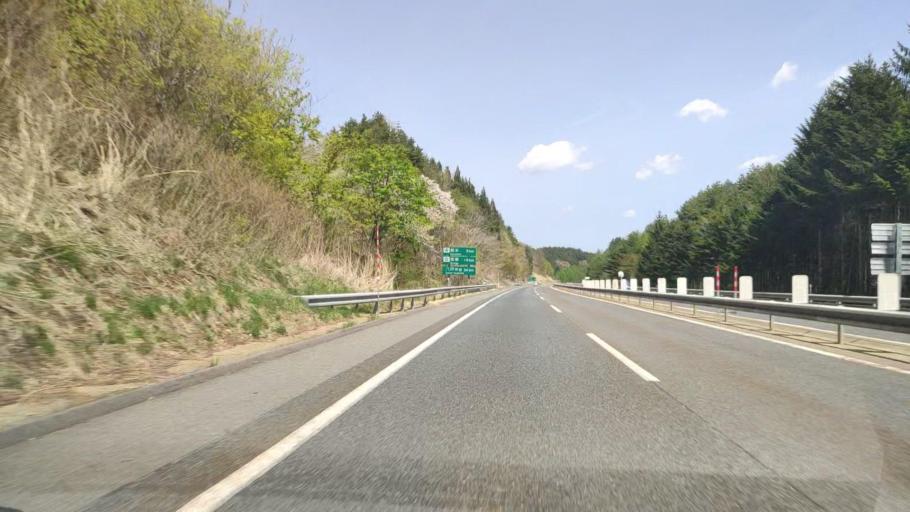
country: JP
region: Iwate
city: Ichinohe
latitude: 40.2677
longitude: 141.3993
